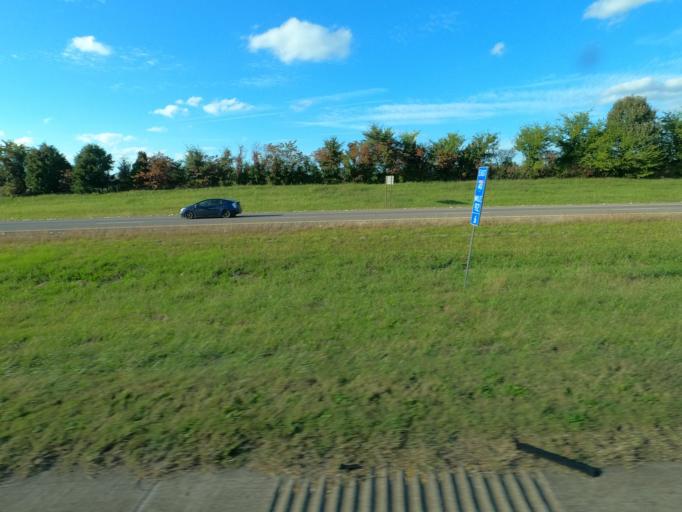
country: US
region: Tennessee
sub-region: Gibson County
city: Medina
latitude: 35.7137
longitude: -88.6480
